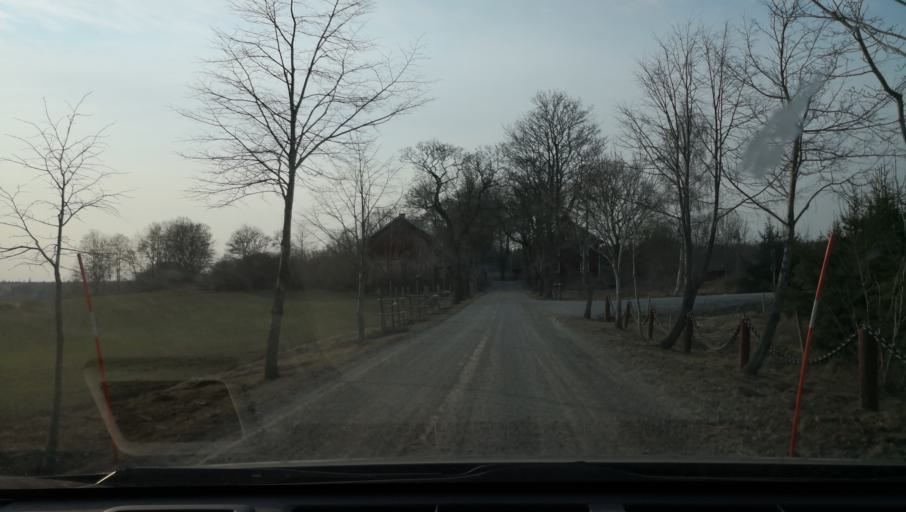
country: SE
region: OErebro
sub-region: Orebro Kommun
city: Hovsta
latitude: 59.3879
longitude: 15.2590
